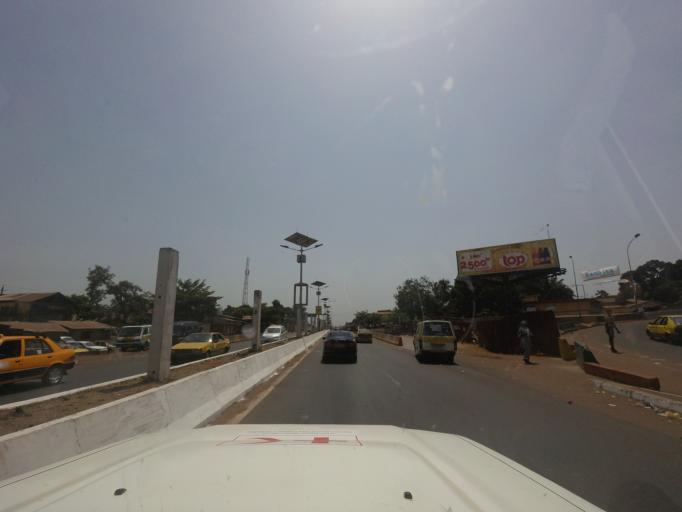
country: GN
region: Conakry
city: Conakry
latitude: 9.5671
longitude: -13.6337
